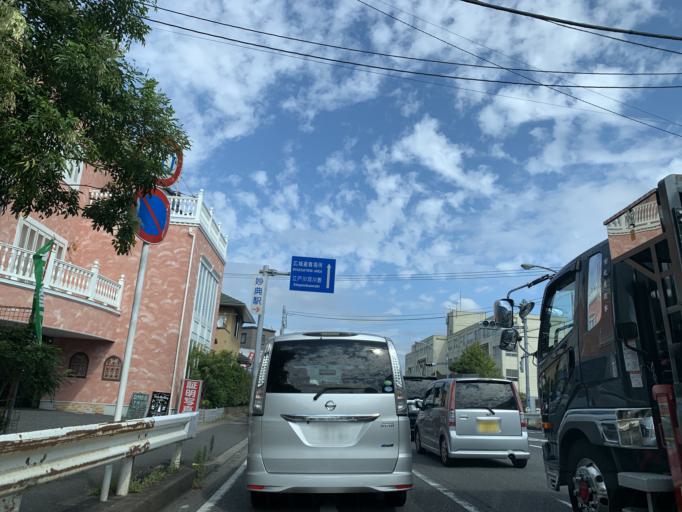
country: JP
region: Tokyo
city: Urayasu
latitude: 35.6916
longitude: 139.9228
